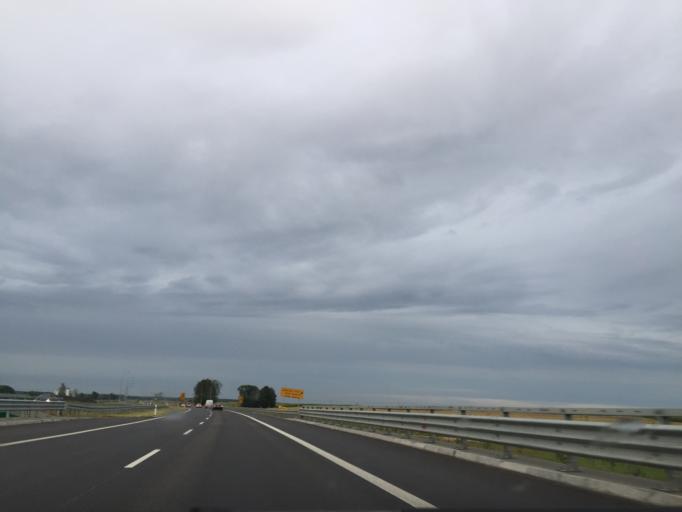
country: PL
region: Podlasie
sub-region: Powiat zambrowski
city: Rutki-Kossaki
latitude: 53.0872
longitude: 22.4861
